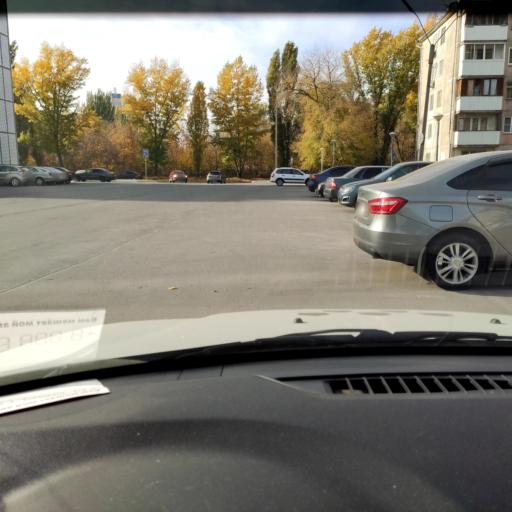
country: RU
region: Samara
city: Tol'yatti
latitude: 53.5205
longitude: 49.4205
